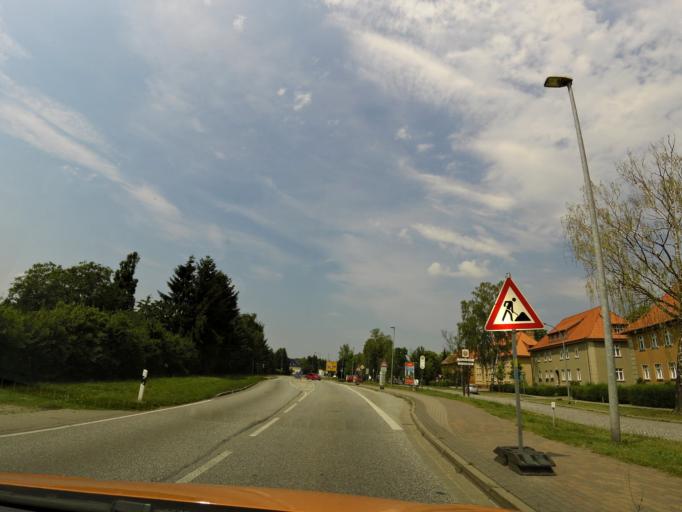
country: DE
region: Brandenburg
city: Kyritz
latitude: 52.9392
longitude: 12.4064
